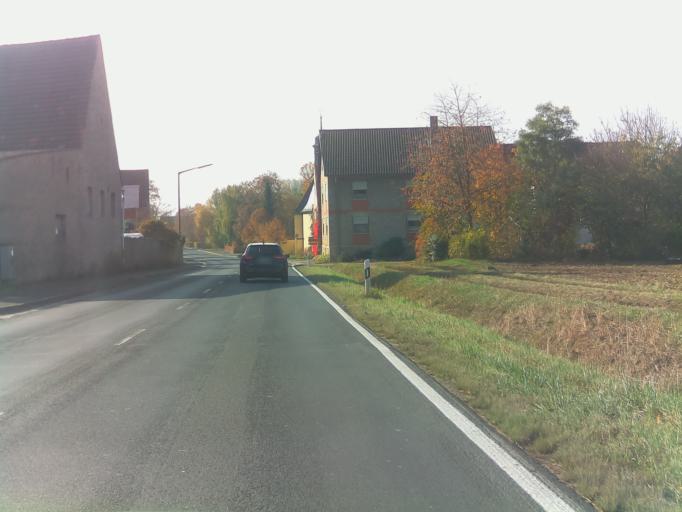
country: DE
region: Bavaria
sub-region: Regierungsbezirk Unterfranken
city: Kleinlangheim
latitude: 49.8040
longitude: 10.2570
